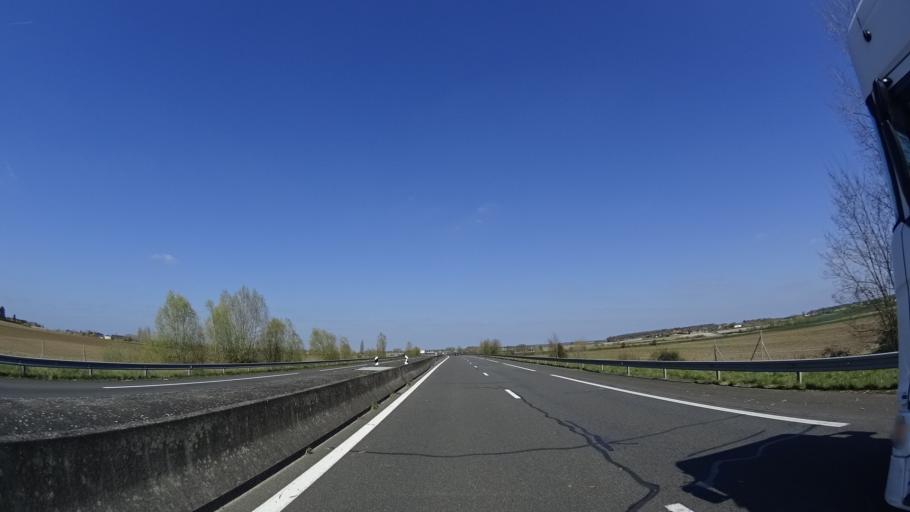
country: FR
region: Pays de la Loire
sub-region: Departement de Maine-et-Loire
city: Saint-Jean
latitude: 47.2621
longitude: -0.3342
